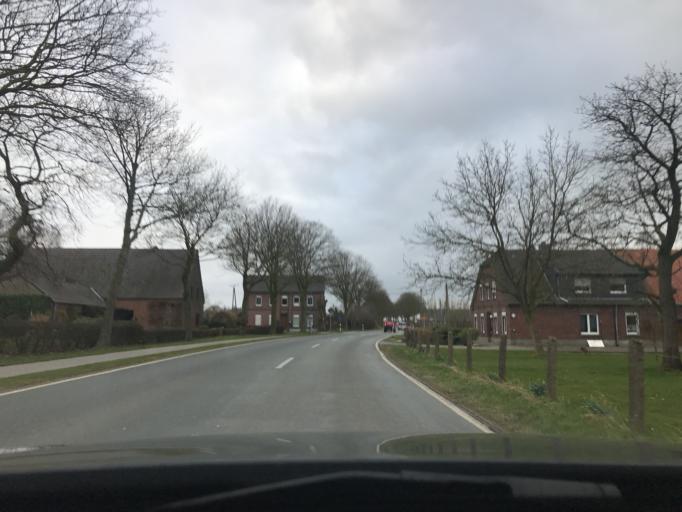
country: DE
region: North Rhine-Westphalia
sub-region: Regierungsbezirk Dusseldorf
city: Goch
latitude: 51.7409
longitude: 6.1990
